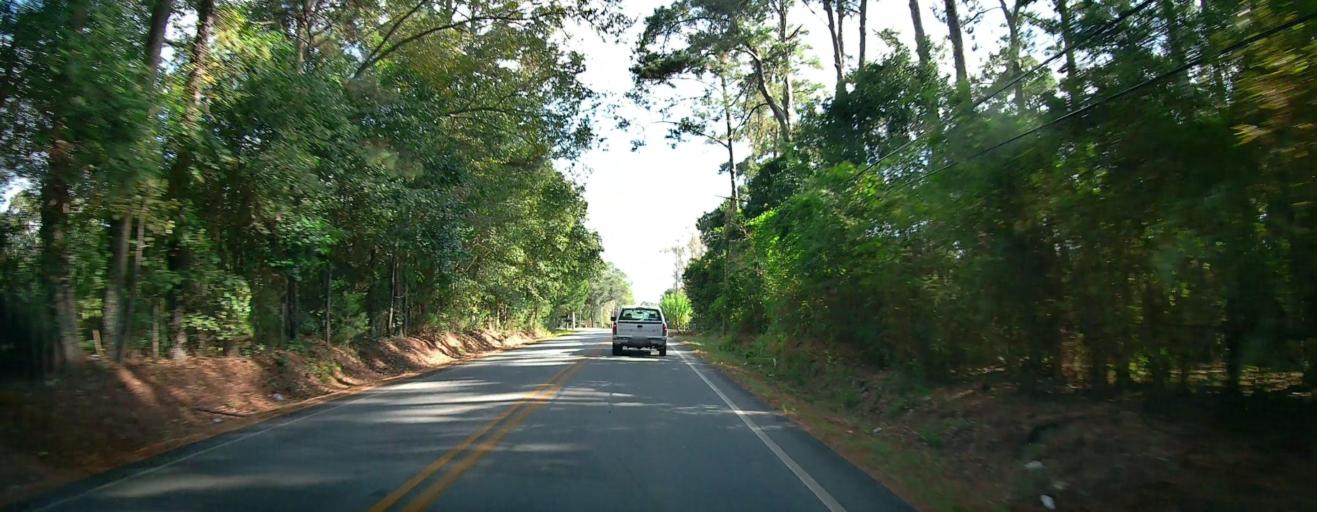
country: US
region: Georgia
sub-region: Thomas County
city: Thomasville
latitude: 30.8747
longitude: -84.0049
